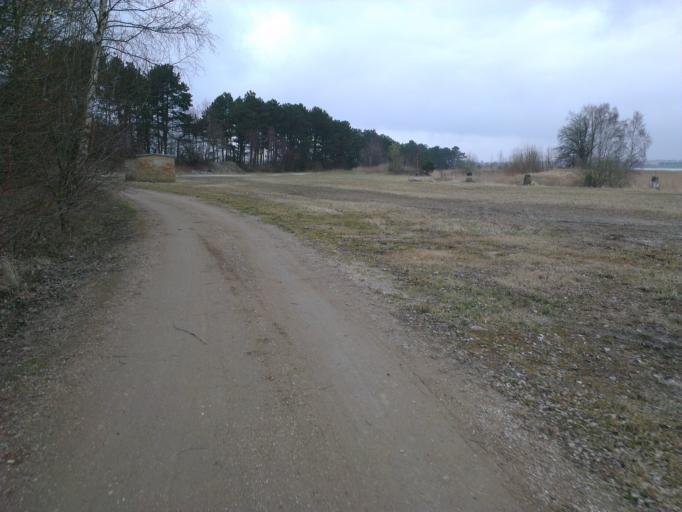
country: DK
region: Capital Region
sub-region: Frederikssund Kommune
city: Frederikssund
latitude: 55.8270
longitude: 12.0349
